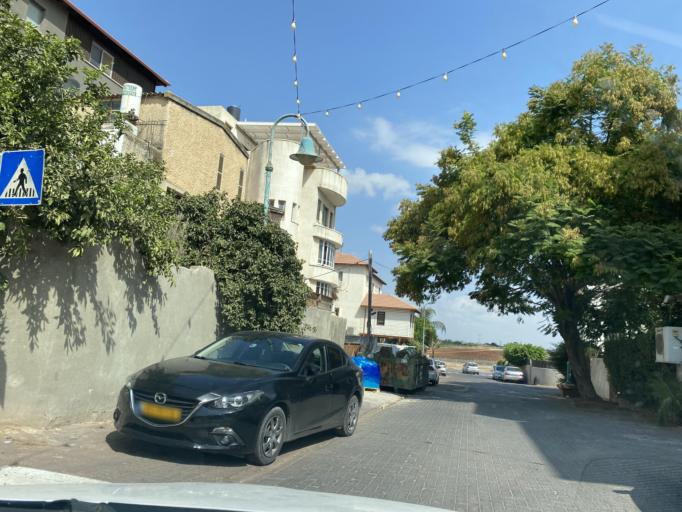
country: IL
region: Central District
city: Jaljulya
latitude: 32.1554
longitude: 34.9530
